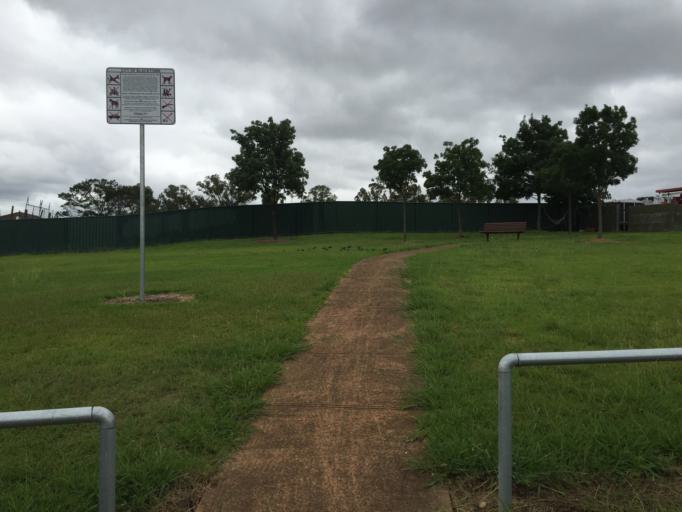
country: AU
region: New South Wales
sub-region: Blacktown
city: Blacktown
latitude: -33.7919
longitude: 150.8993
